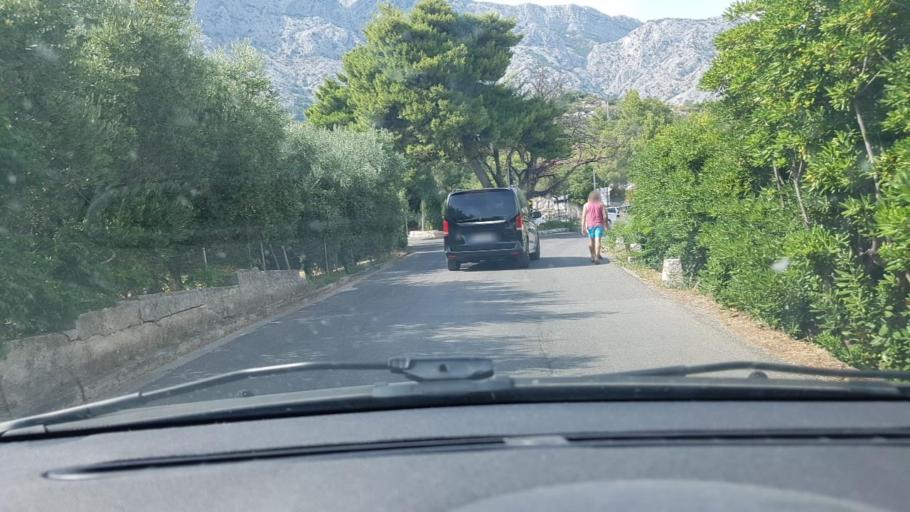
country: HR
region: Dubrovacko-Neretvanska
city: Orebic
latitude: 42.9752
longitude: 17.1688
